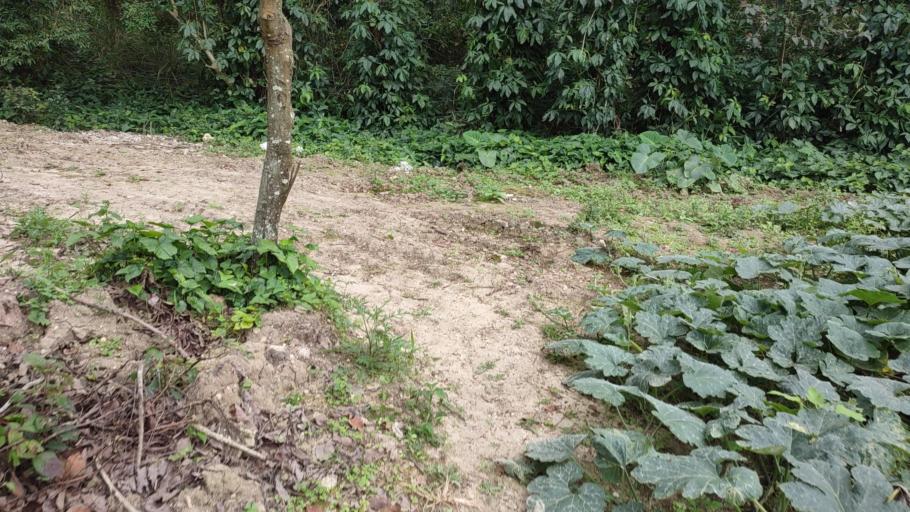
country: MX
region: Veracruz
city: Papantla de Olarte
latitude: 20.4641
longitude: -97.3364
